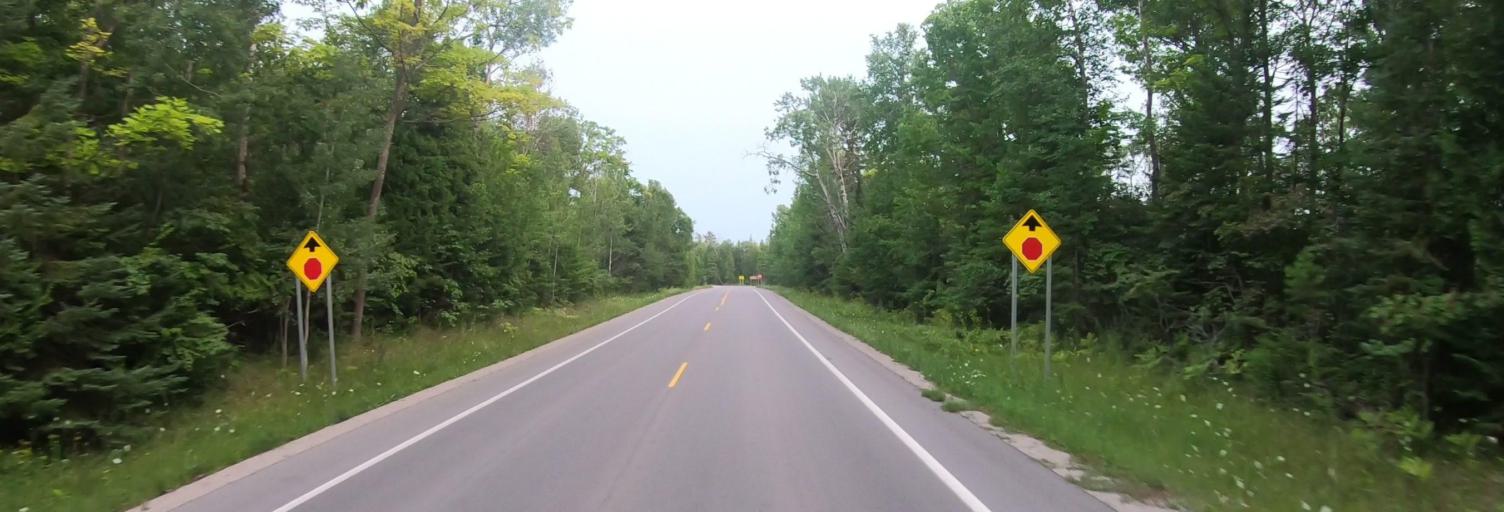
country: US
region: Michigan
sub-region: Mackinac County
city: Saint Ignace
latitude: 45.7688
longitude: -84.7730
